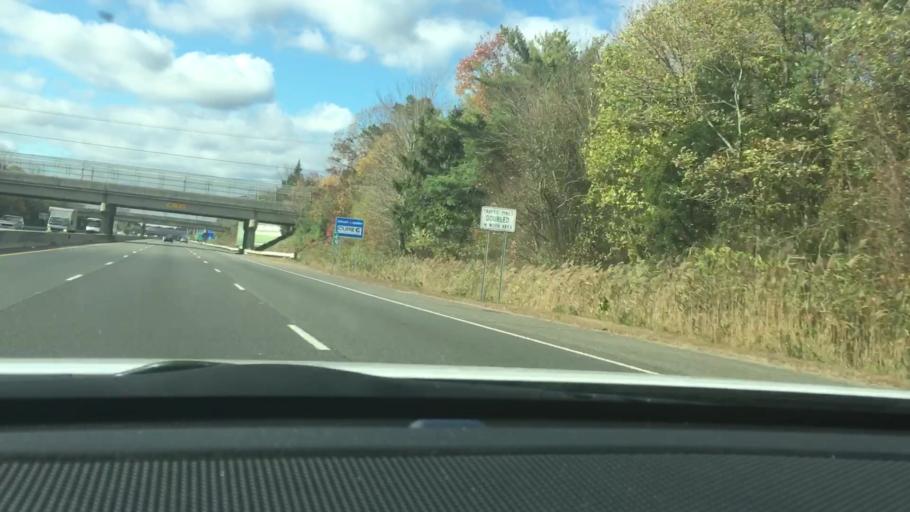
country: US
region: New Jersey
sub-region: Atlantic County
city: Pleasantville
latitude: 39.3977
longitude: -74.5157
